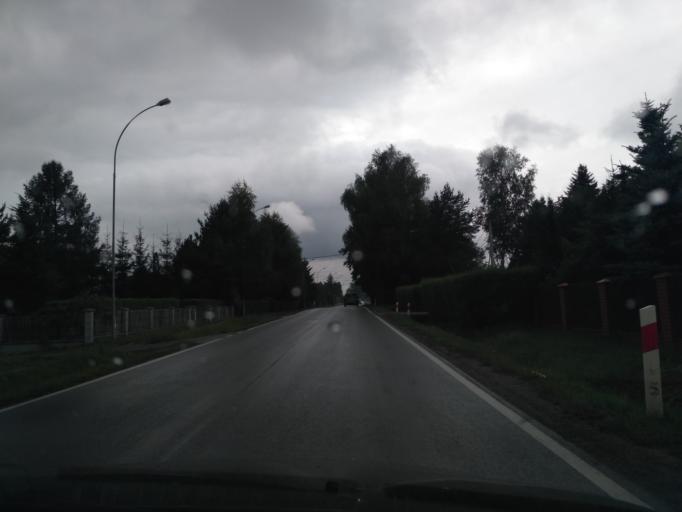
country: PL
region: Subcarpathian Voivodeship
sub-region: Powiat krosnienski
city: Korczyna
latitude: 49.7114
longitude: 21.7928
